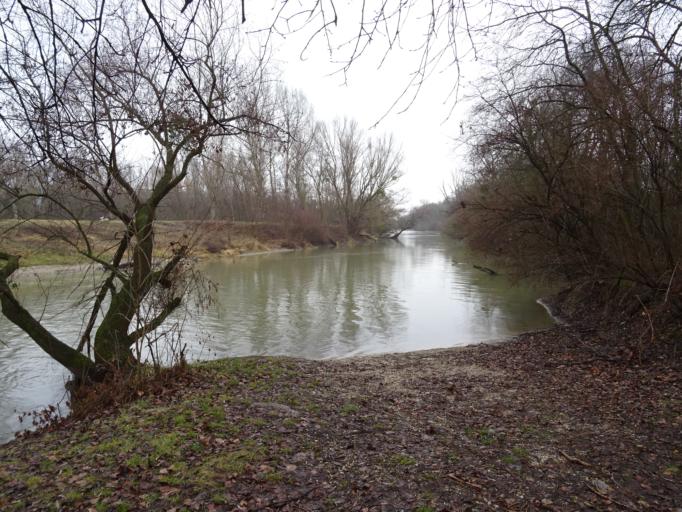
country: HU
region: Gyor-Moson-Sopron
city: Rajka
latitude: 47.9903
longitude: 17.2380
